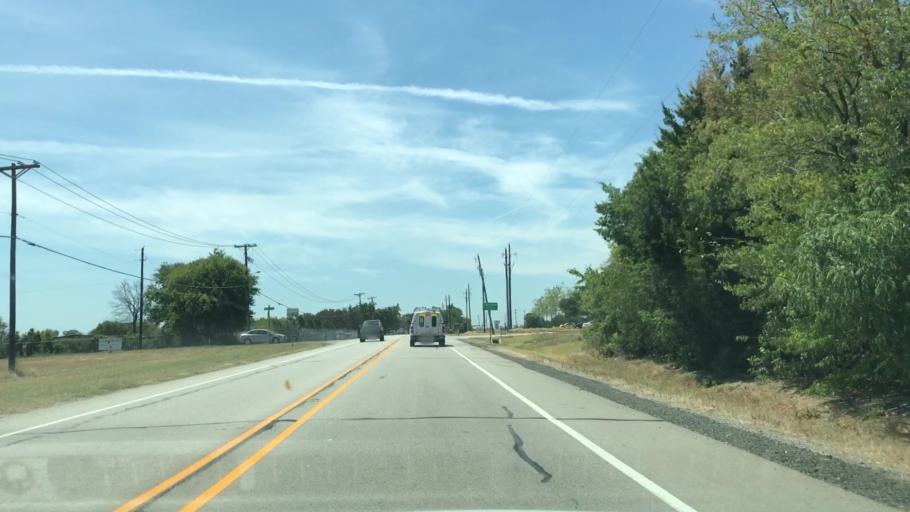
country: US
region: Texas
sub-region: Collin County
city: Fairview
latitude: 33.1623
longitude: -96.6306
